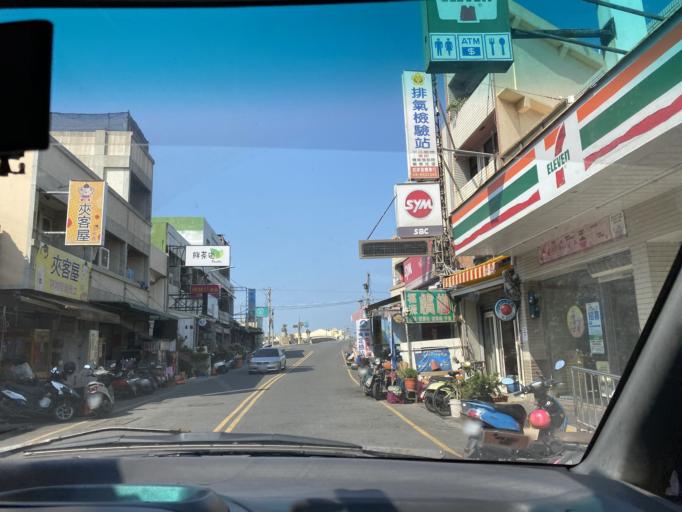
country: TW
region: Taiwan
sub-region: Changhua
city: Chang-hua
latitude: 23.9655
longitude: 120.3409
